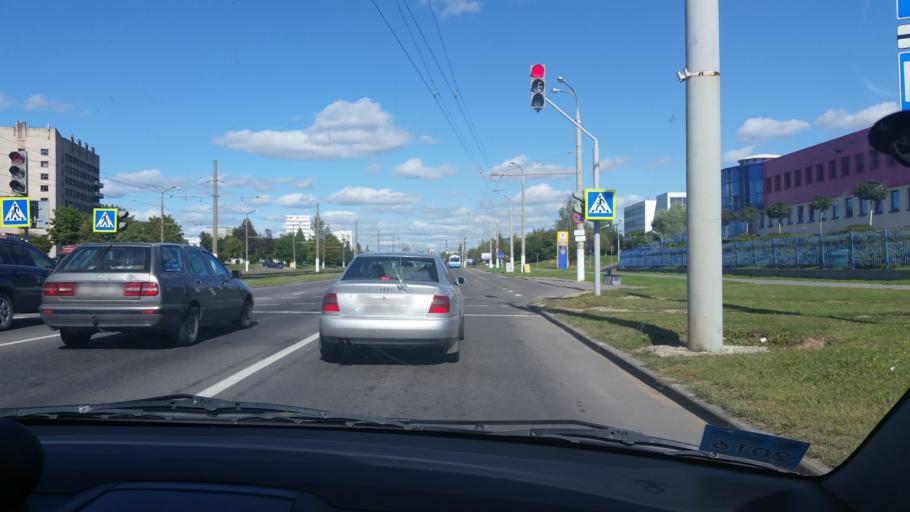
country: BY
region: Vitebsk
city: Vitebsk
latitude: 55.1601
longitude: 30.2361
